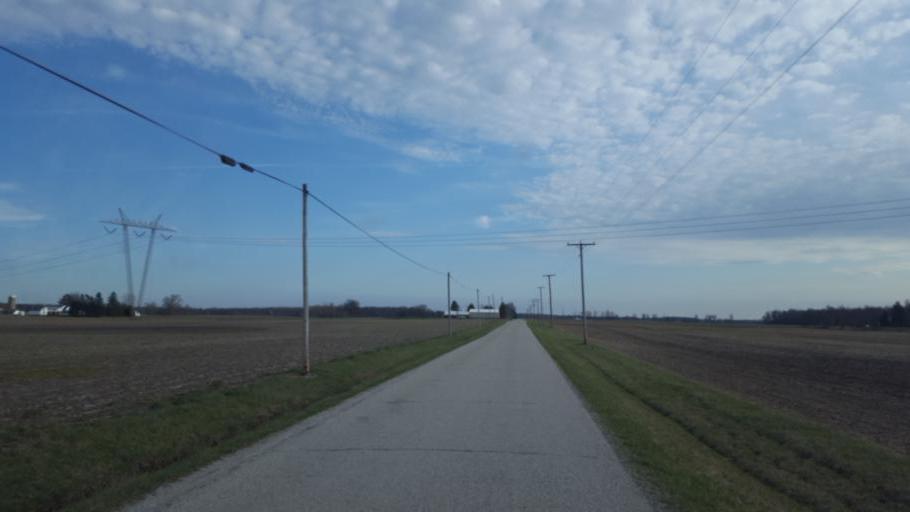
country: US
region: Ohio
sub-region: Crawford County
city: Bucyrus
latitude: 40.7451
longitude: -82.9374
